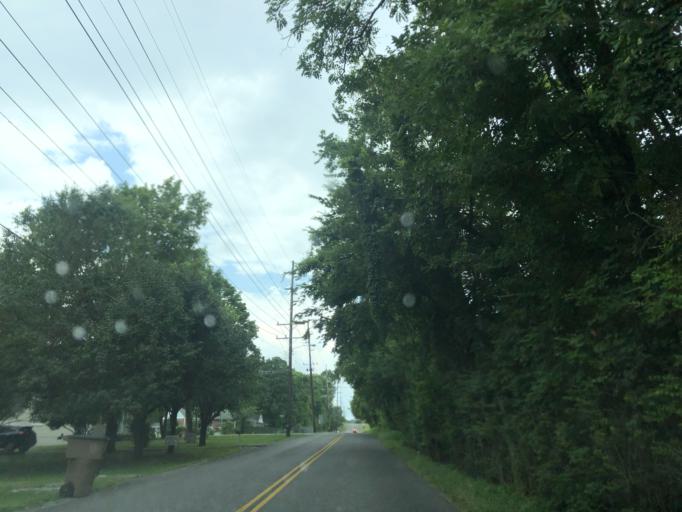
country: US
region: Tennessee
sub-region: Davidson County
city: Lakewood
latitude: 36.1630
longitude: -86.6554
